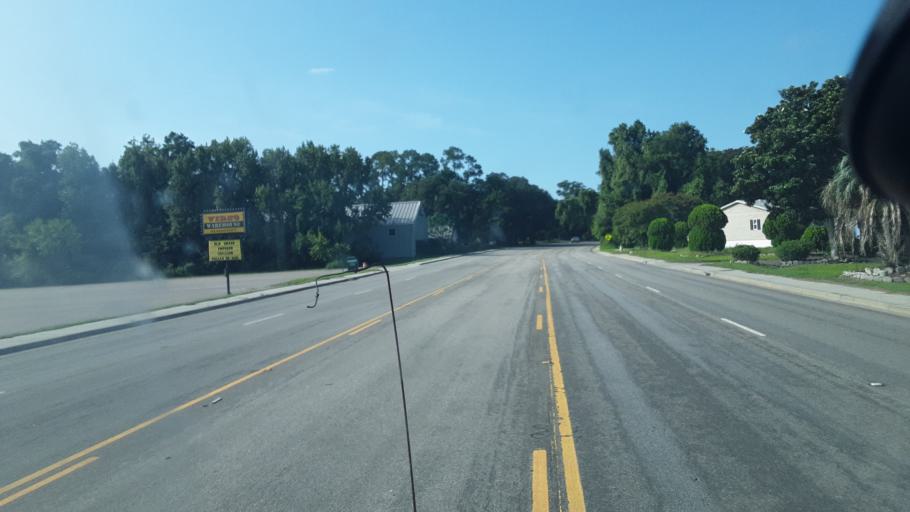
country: US
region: South Carolina
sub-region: Beaufort County
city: Shell Point
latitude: 32.4036
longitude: -80.7357
